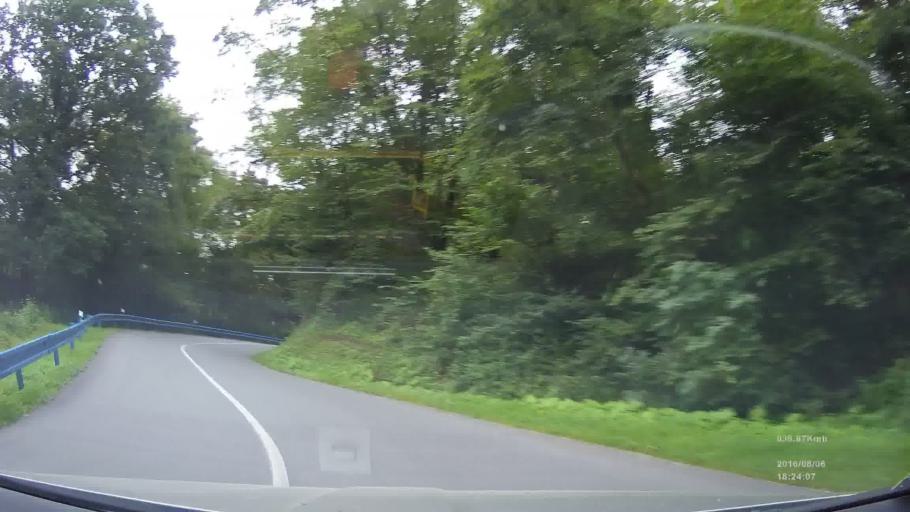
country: SK
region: Presovsky
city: Svidnik
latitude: 49.2971
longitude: 21.5688
